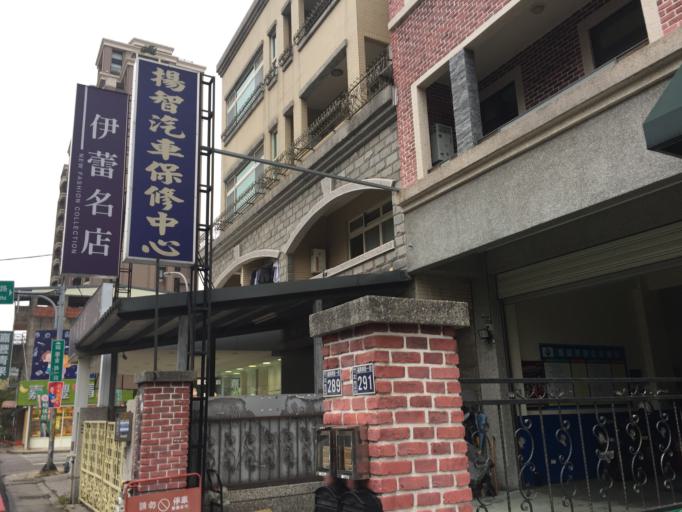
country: TW
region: Taiwan
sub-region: Hsinchu
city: Zhubei
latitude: 24.8182
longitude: 121.0235
